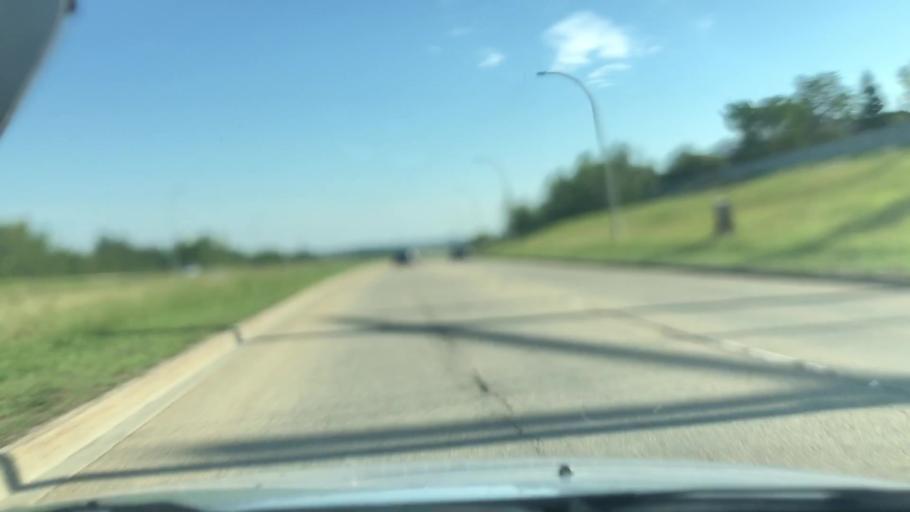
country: CA
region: Alberta
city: Edmonton
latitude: 53.4618
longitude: -113.5868
